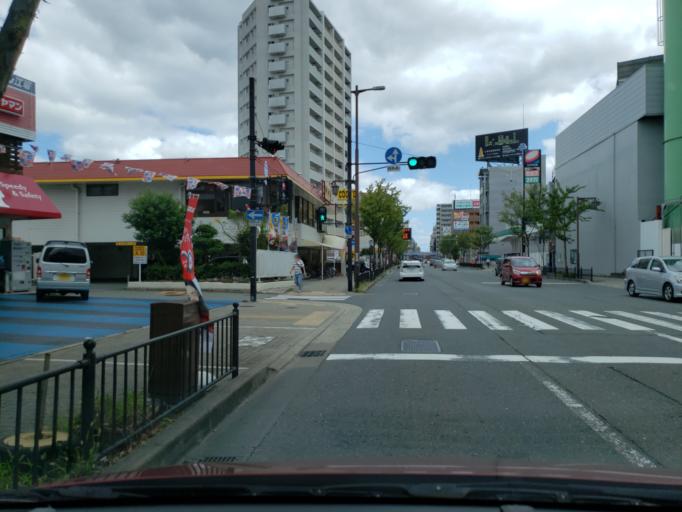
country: JP
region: Osaka
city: Suita
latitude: 34.7576
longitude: 135.4896
